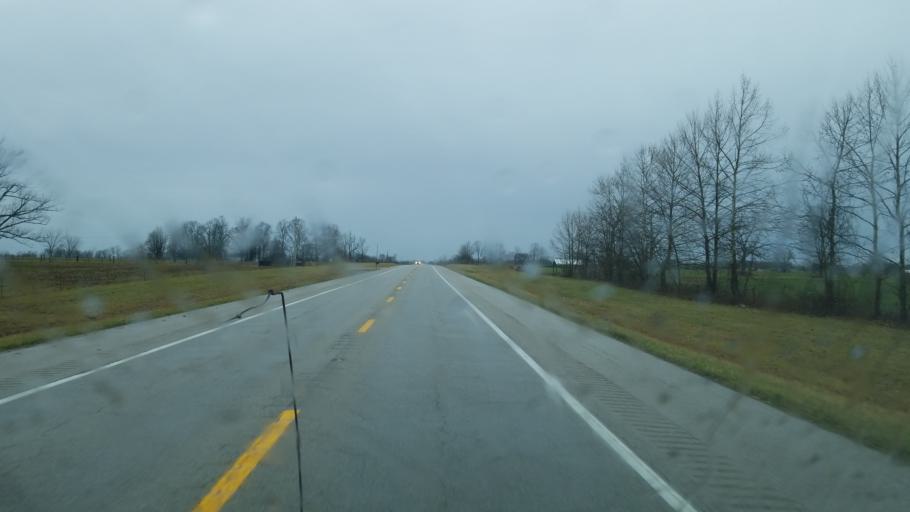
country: US
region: Ohio
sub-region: Adams County
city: Manchester
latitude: 38.5599
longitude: -83.6039
